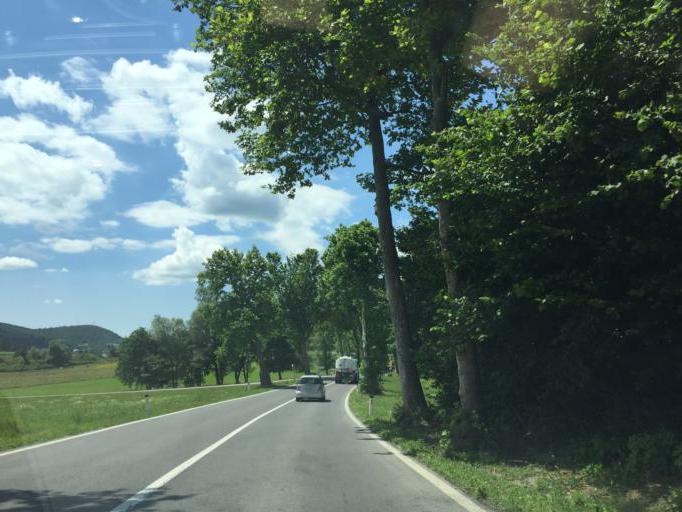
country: SI
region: Postojna
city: Postojna
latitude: 45.7608
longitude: 14.0833
